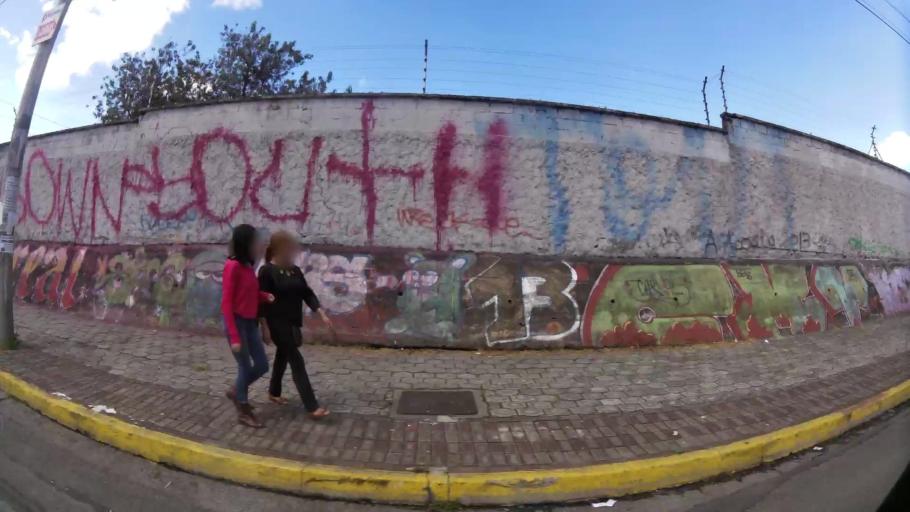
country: EC
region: Pichincha
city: Quito
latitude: -0.2998
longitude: -78.5425
